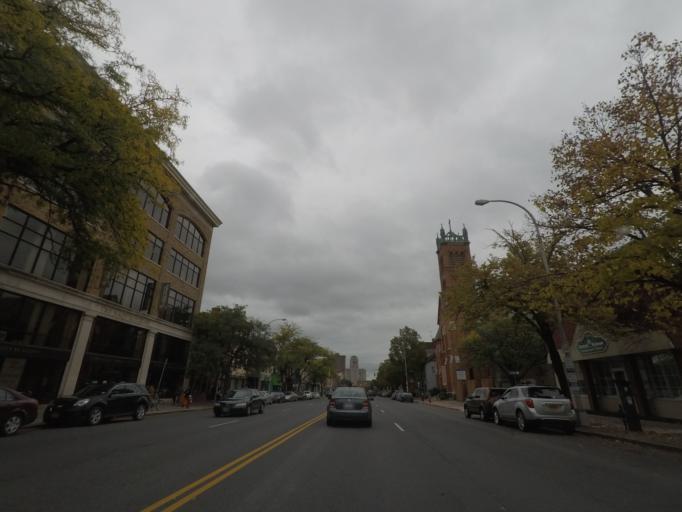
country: US
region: New York
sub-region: Albany County
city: Albany
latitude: 42.6618
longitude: -73.7690
